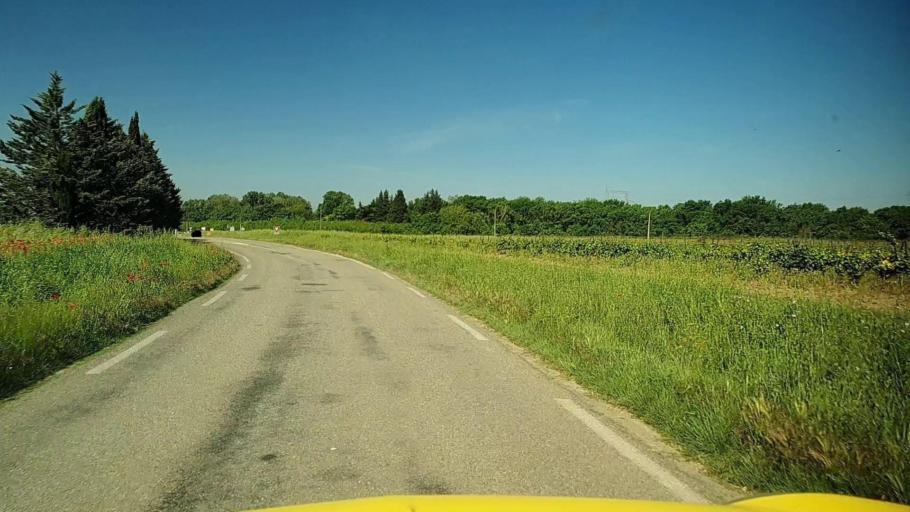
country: FR
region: Languedoc-Roussillon
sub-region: Departement du Gard
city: Saint-Chaptes
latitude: 43.9424
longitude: 4.3172
